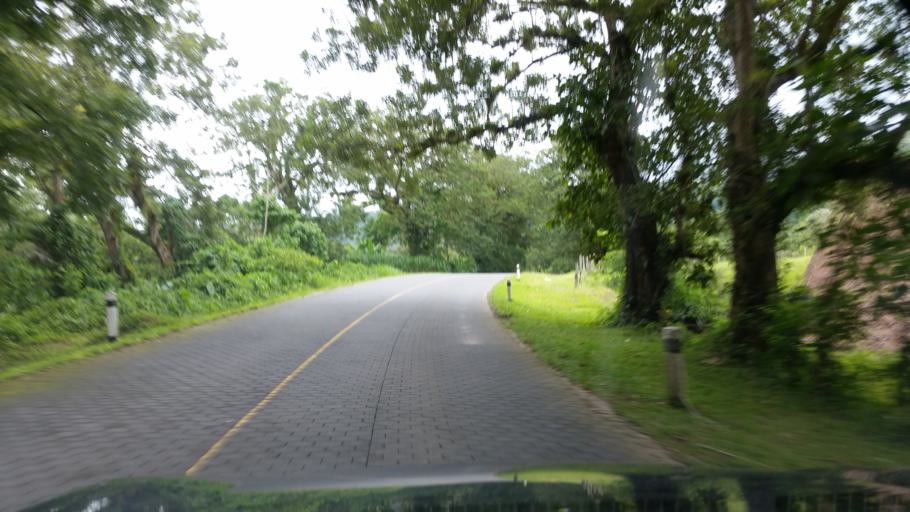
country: NI
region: Jinotega
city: Jinotega
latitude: 13.1914
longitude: -85.7326
